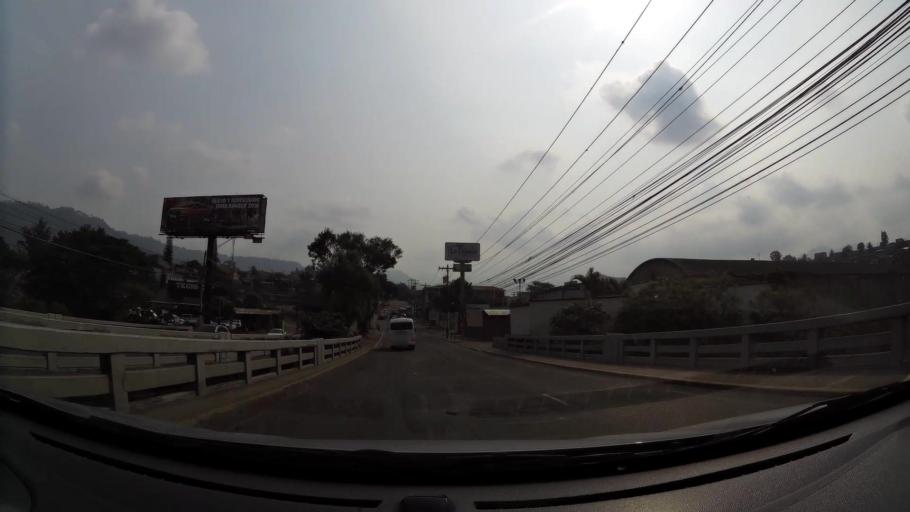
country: HN
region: Francisco Morazan
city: Tegucigalpa
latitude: 14.1037
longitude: -87.1748
